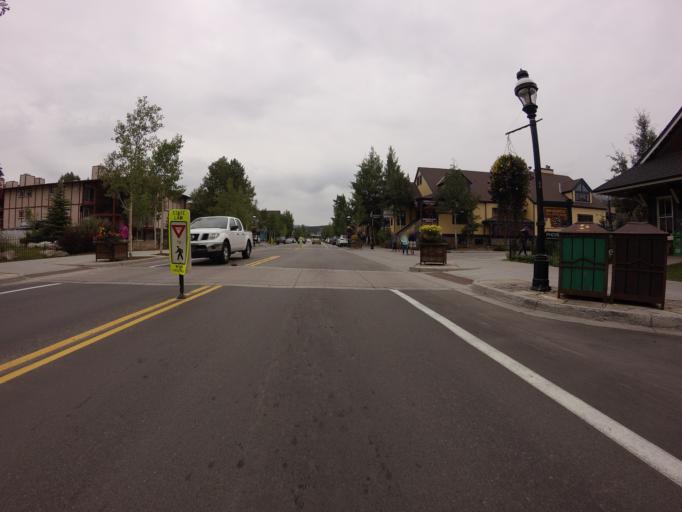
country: US
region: Colorado
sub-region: Summit County
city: Breckenridge
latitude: 39.4847
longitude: -106.0462
